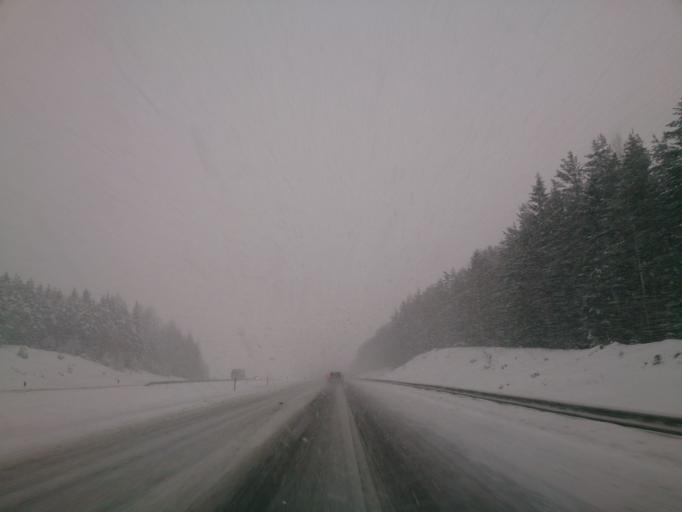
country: SE
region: Soedermanland
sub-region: Nykopings Kommun
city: Stigtomta
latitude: 58.7568
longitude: 16.7192
